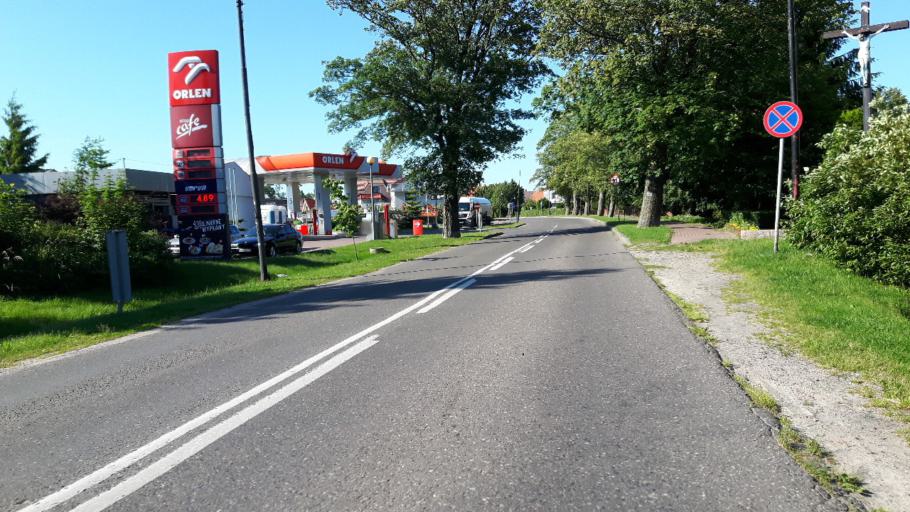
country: PL
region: Pomeranian Voivodeship
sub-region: Powiat leborski
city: Leba
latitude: 54.7511
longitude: 17.5582
